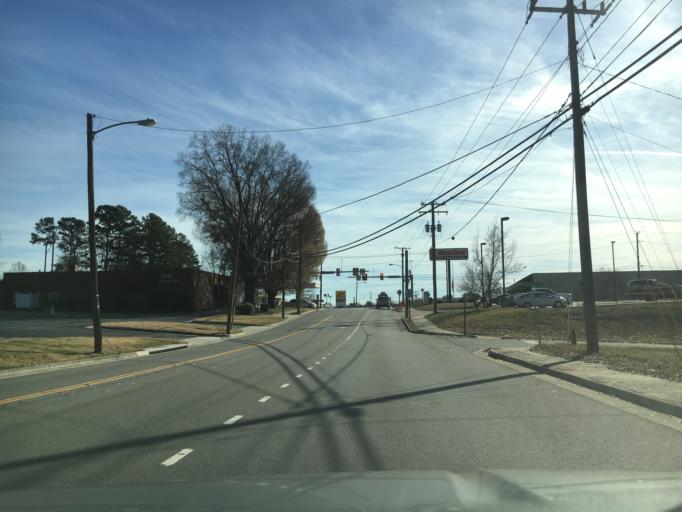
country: US
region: Virginia
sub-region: Halifax County
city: South Boston
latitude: 36.7073
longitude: -78.9106
